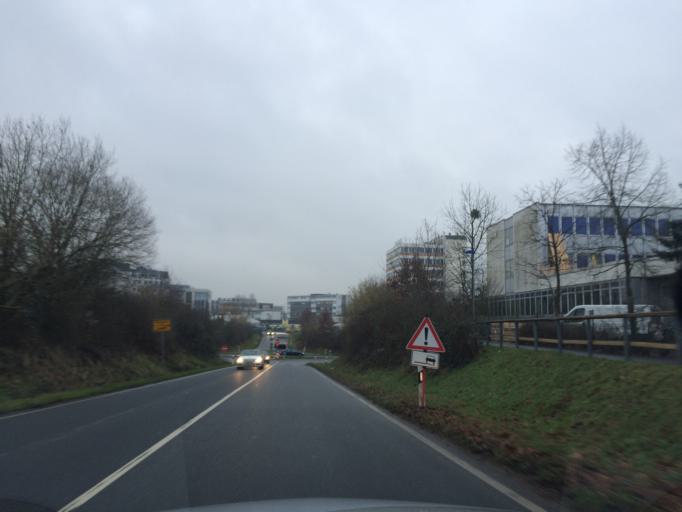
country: DE
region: Hesse
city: Langen
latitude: 49.9993
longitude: 8.6492
